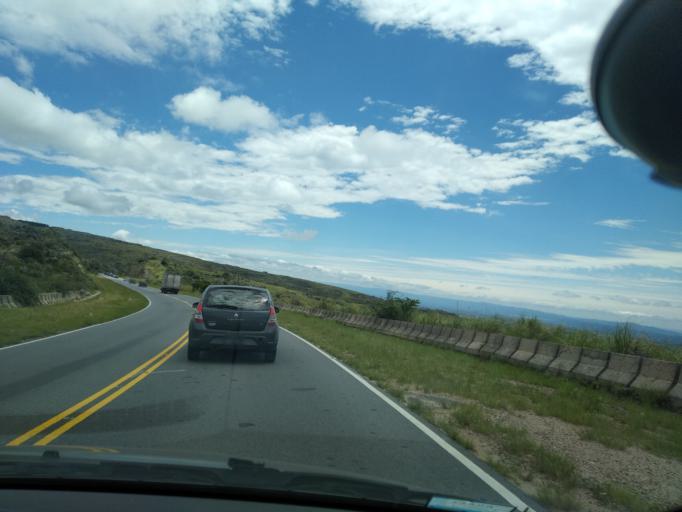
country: AR
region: Cordoba
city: Cuesta Blanca
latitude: -31.6367
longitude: -64.6764
